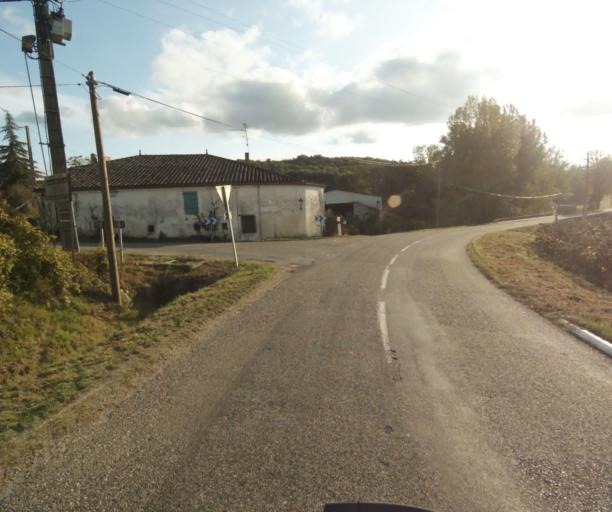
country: FR
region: Midi-Pyrenees
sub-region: Departement de la Haute-Garonne
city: Launac
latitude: 43.8196
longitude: 1.1339
